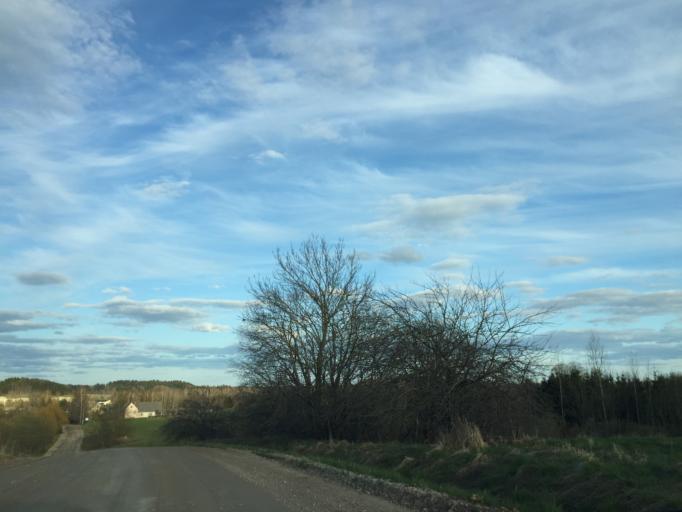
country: LV
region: Rezekne
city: Rezekne
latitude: 56.5730
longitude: 27.3524
